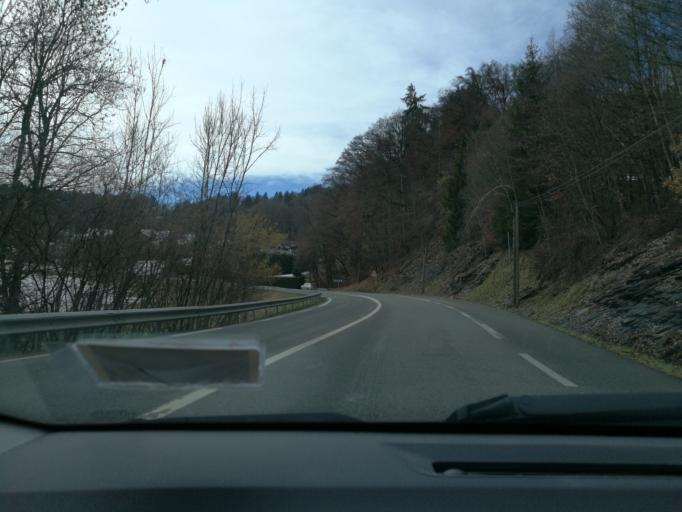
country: FR
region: Rhone-Alpes
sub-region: Departement de la Haute-Savoie
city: Domancy
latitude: 45.9162
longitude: 6.6363
